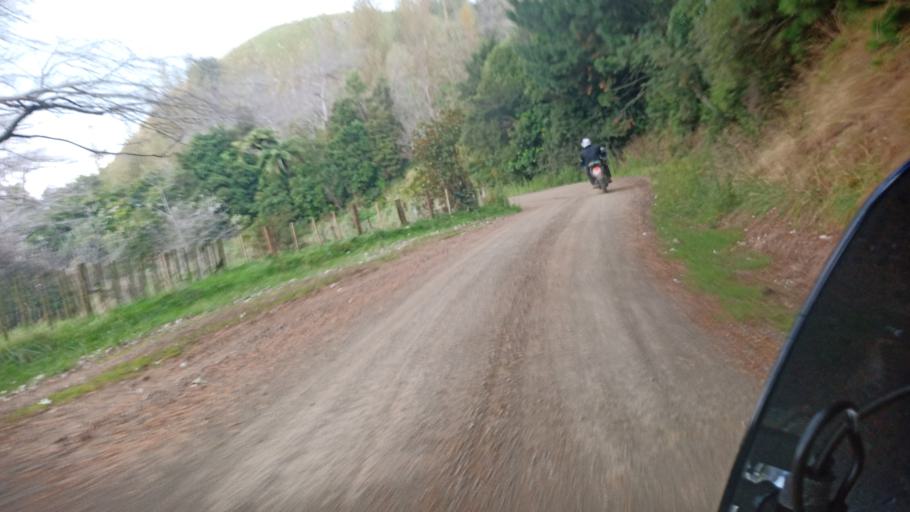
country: NZ
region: Gisborne
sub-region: Gisborne District
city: Gisborne
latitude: -38.4757
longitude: 177.6147
